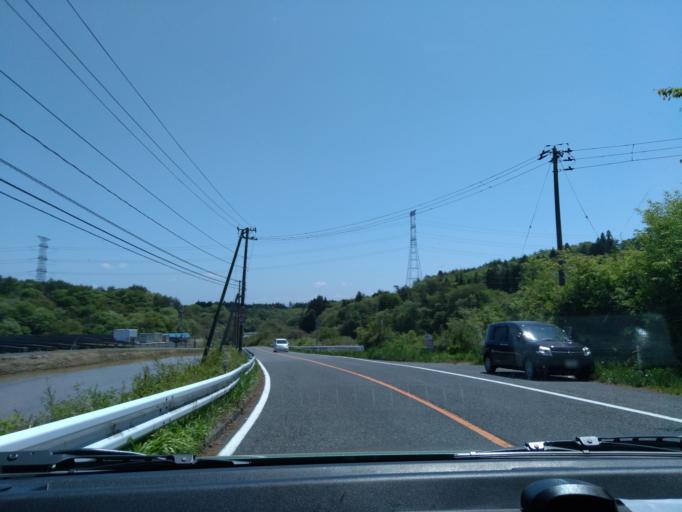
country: JP
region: Iwate
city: Ichinoseki
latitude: 38.8710
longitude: 141.1483
